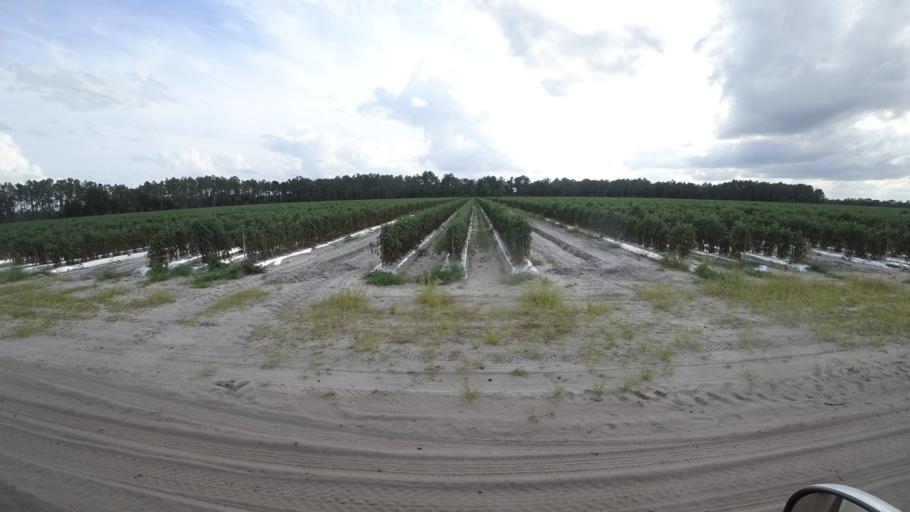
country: US
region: Florida
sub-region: Hillsborough County
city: Balm
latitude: 27.6236
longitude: -82.1299
